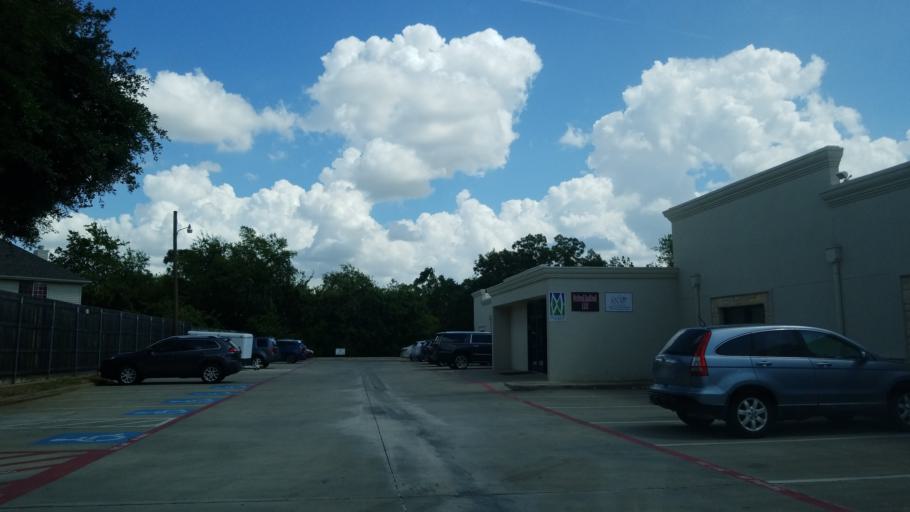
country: US
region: Texas
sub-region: Tarrant County
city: Euless
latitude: 32.8486
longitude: -97.0969
